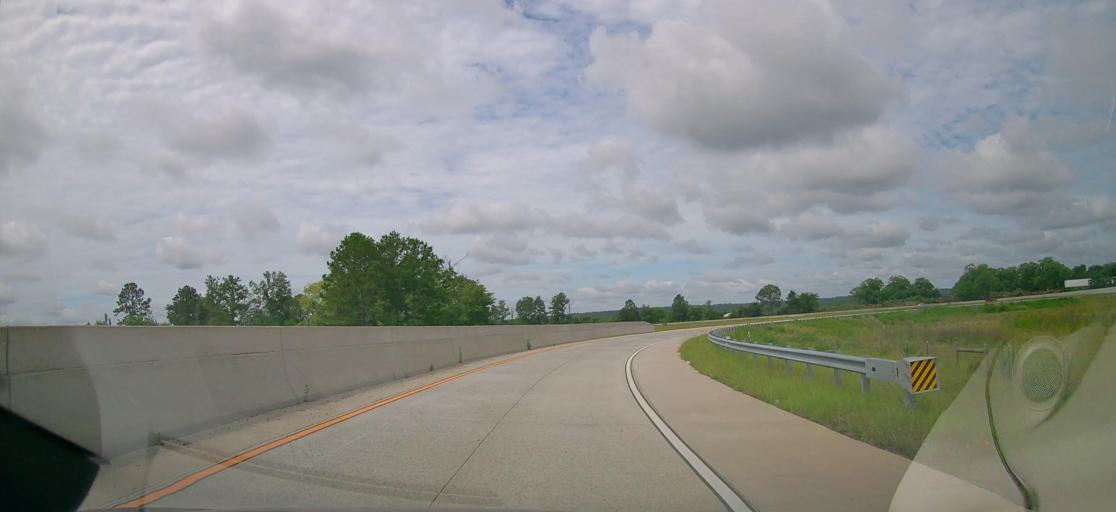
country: US
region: Georgia
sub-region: Houston County
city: Warner Robins
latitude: 32.6813
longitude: -83.6284
